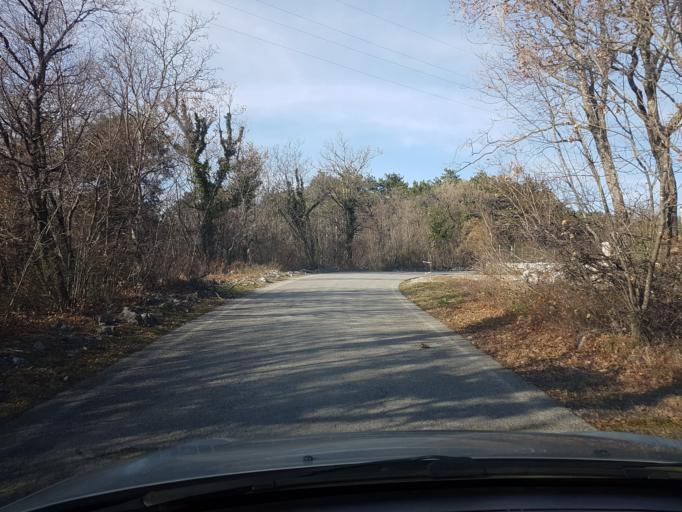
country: IT
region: Friuli Venezia Giulia
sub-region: Provincia di Trieste
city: Sistiana-Visogliano
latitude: 45.7818
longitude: 13.6404
